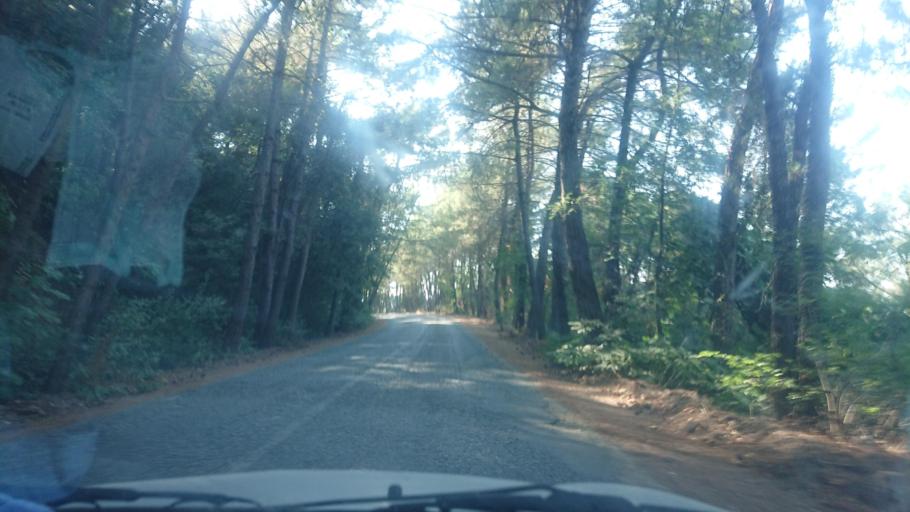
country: TR
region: Aydin
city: Atburgazi
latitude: 37.6909
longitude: 27.1523
